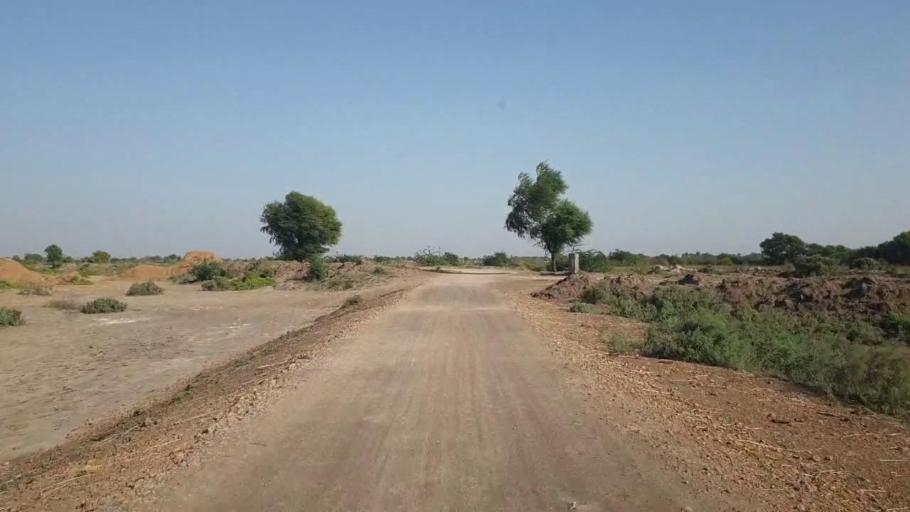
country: PK
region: Sindh
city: Rajo Khanani
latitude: 25.0085
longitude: 68.7793
